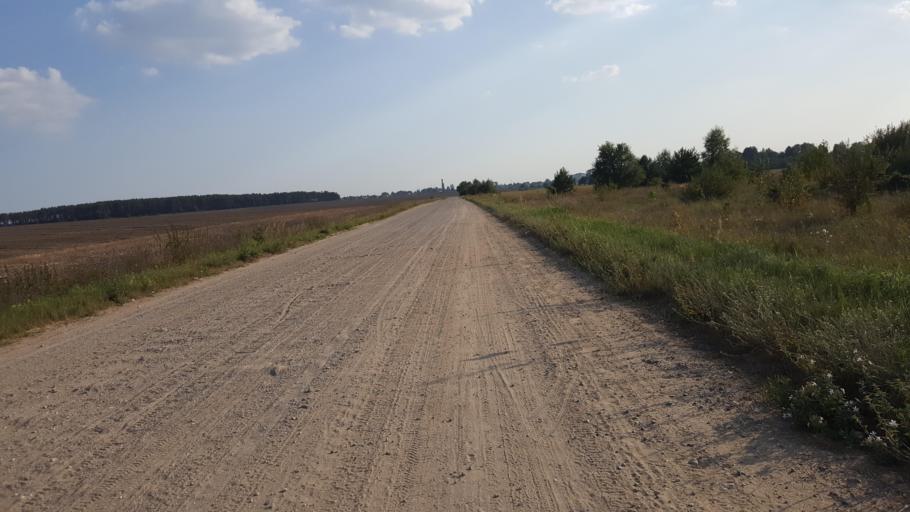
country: BY
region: Brest
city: Kamyanyets
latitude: 52.4190
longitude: 23.8420
